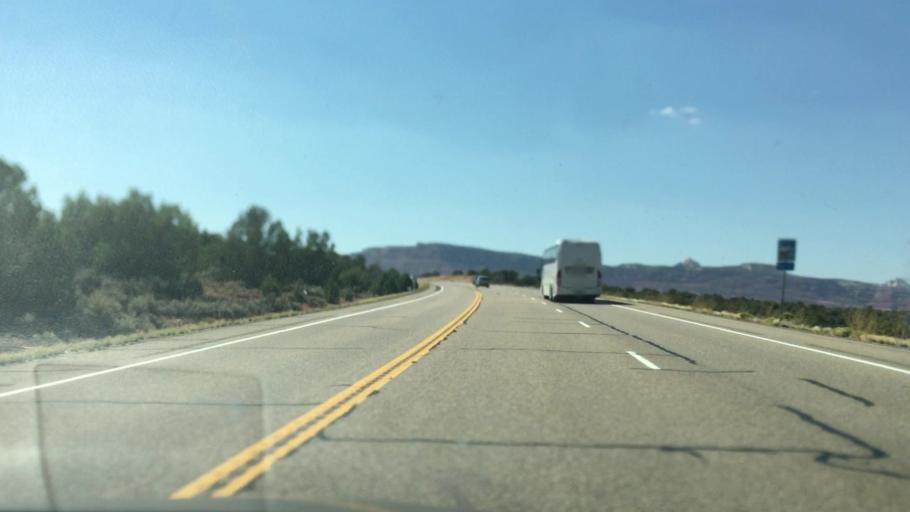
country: US
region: Utah
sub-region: Kane County
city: Kanab
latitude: 37.1844
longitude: -111.9817
